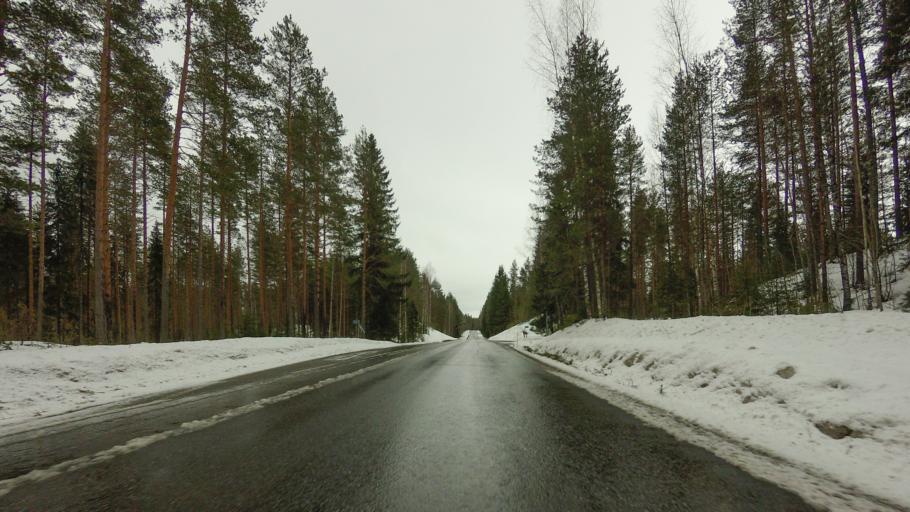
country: FI
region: Southern Savonia
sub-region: Savonlinna
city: Savonlinna
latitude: 61.9823
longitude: 28.8089
